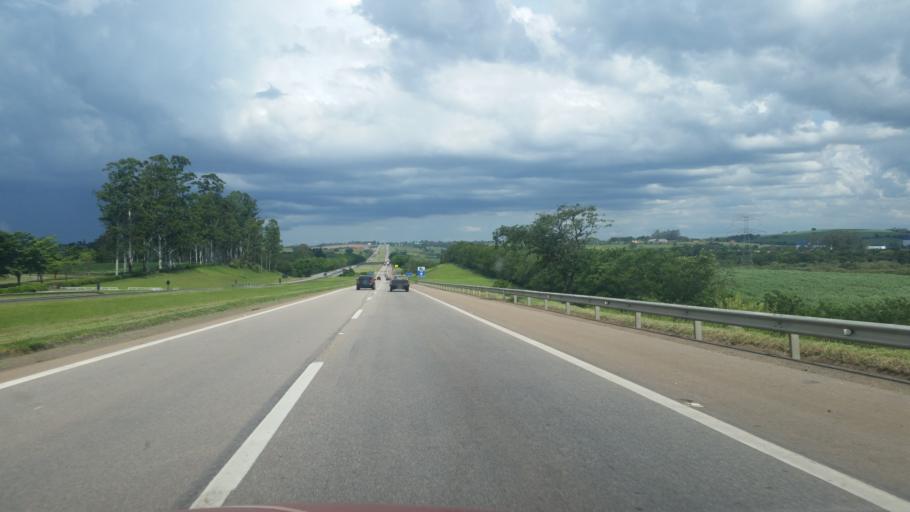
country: BR
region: Sao Paulo
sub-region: Boituva
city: Boituva
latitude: -23.2851
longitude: -47.7754
